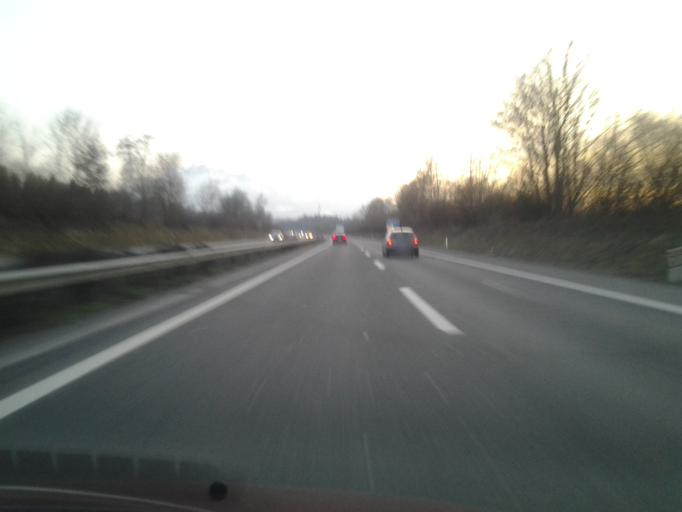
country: CH
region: Lucerne
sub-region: Hochdorf District
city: Inwil
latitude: 47.1152
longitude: 8.3569
